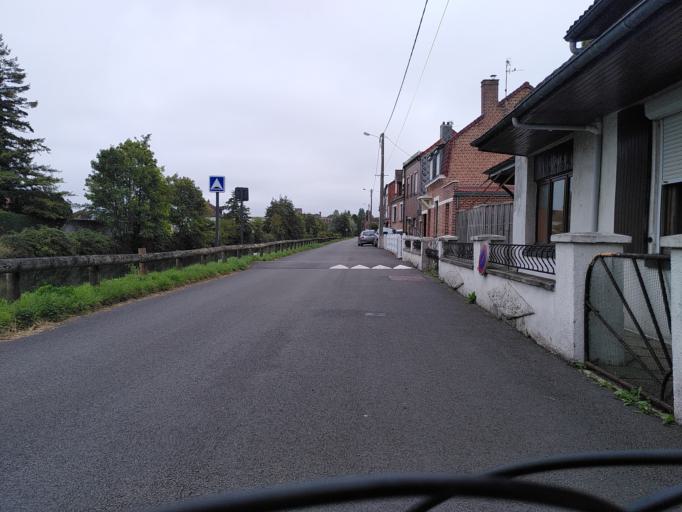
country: FR
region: Nord-Pas-de-Calais
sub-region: Departement du Nord
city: Merville
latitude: 50.6369
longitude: 2.6294
